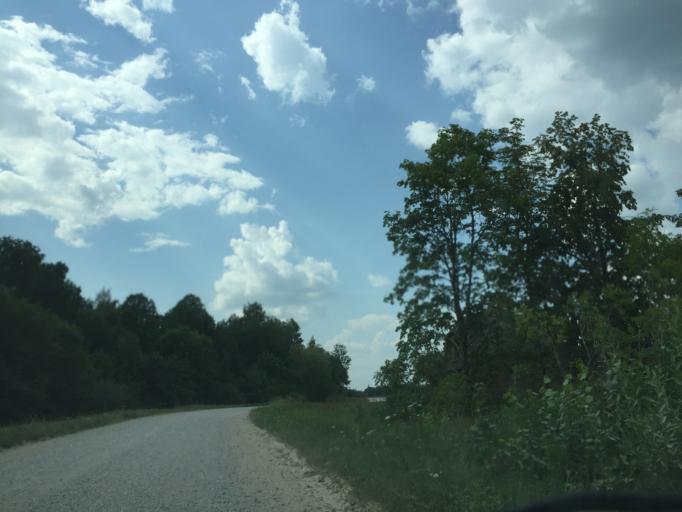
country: LV
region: Auces Novads
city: Auce
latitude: 56.4046
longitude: 23.0477
